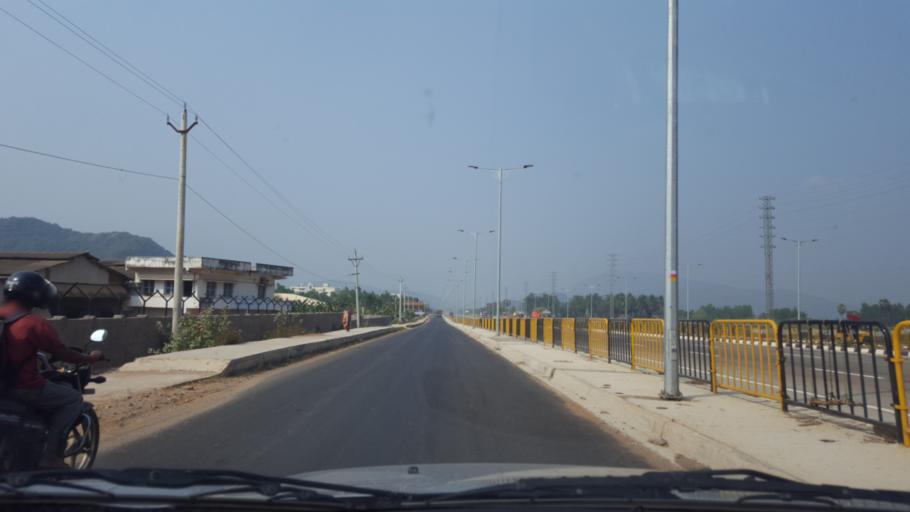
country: IN
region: Andhra Pradesh
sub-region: Vishakhapatnam
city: Bhimunipatnam
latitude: 17.8914
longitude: 83.3662
